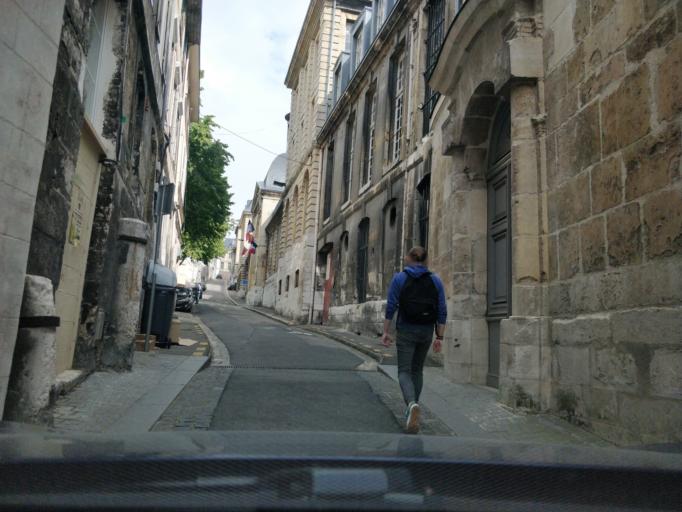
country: FR
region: Haute-Normandie
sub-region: Departement de la Seine-Maritime
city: Rouen
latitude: 49.4448
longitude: 1.0999
